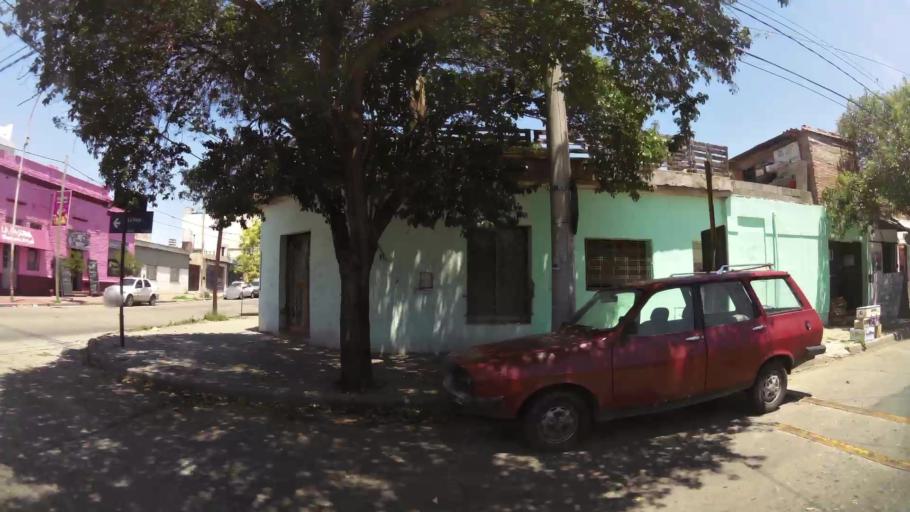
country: AR
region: Cordoba
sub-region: Departamento de Capital
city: Cordoba
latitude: -31.4028
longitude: -64.2119
